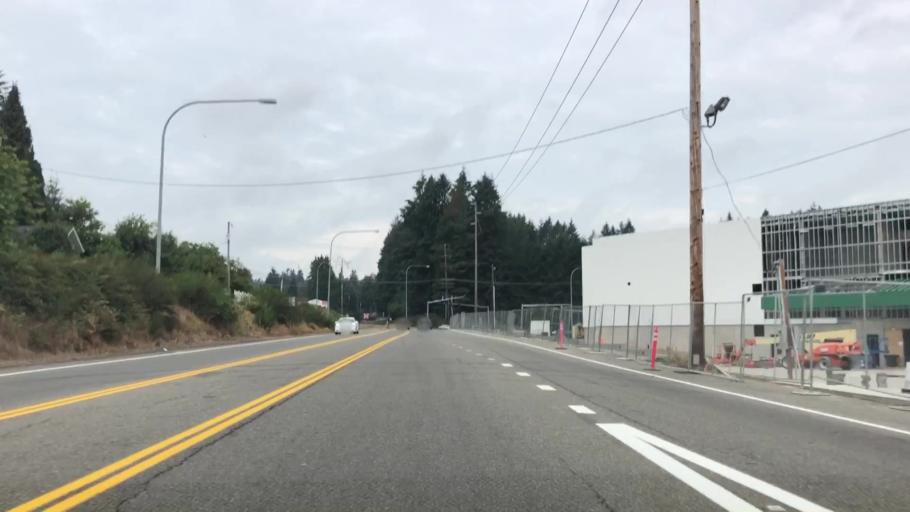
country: US
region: Washington
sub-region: Kitsap County
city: Navy Yard City
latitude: 47.5254
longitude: -122.7024
